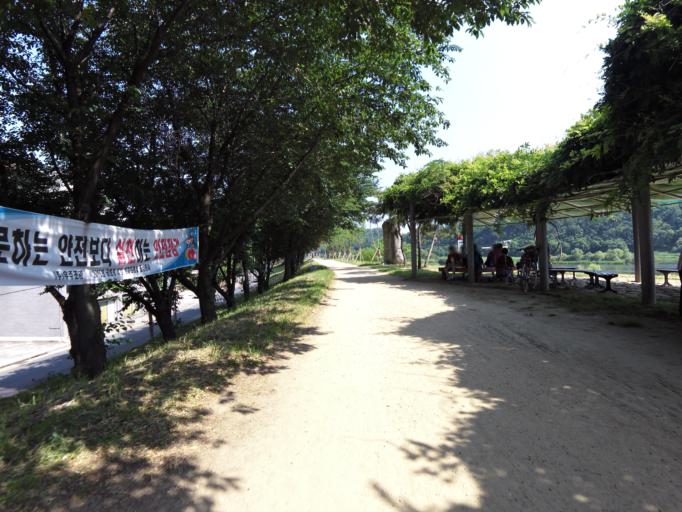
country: KR
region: Daegu
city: Daegu
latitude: 35.8756
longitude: 128.6632
